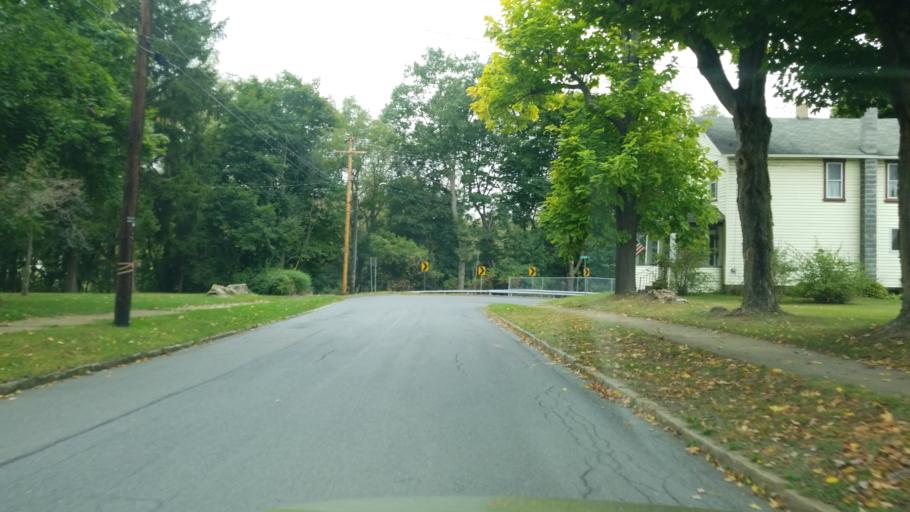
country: US
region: Pennsylvania
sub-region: Clearfield County
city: Curwensville
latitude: 40.9723
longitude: -78.5179
